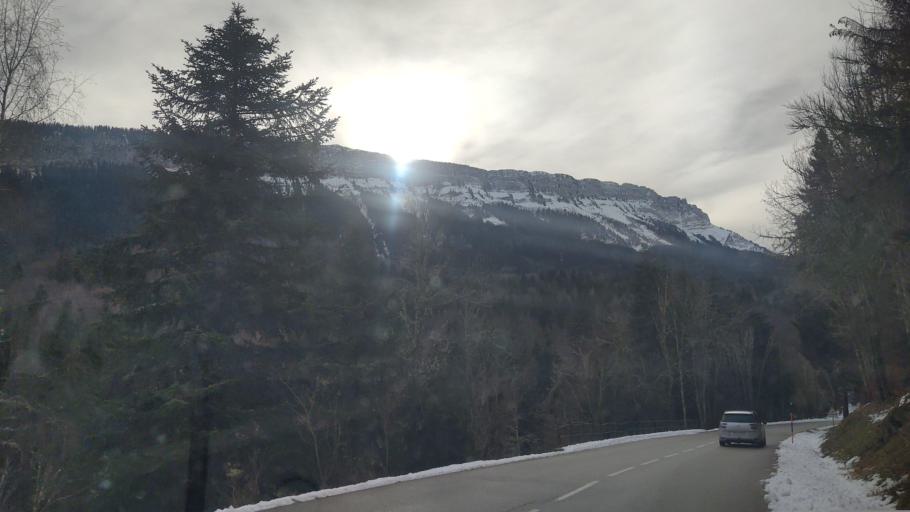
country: FR
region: Rhone-Alpes
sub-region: Departement de la Haute-Savoie
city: Cusy
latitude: 45.6688
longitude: 6.0430
